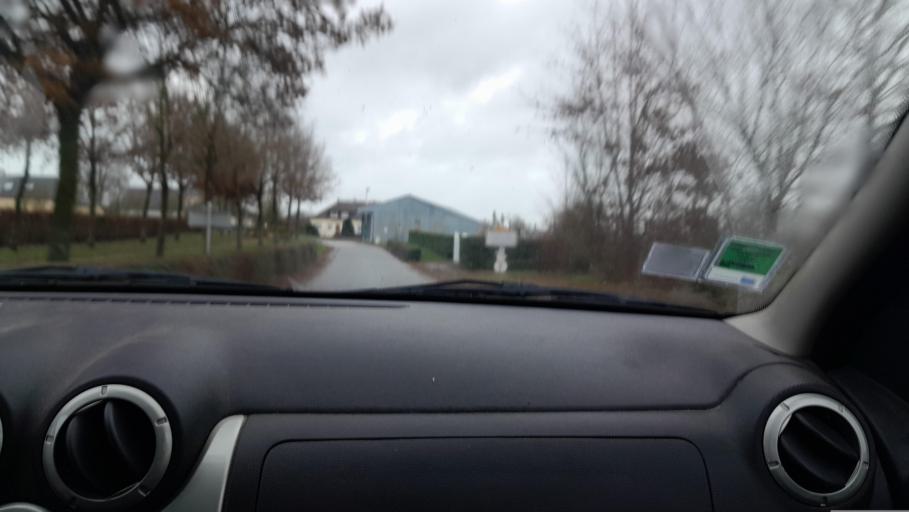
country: FR
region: Pays de la Loire
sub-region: Departement de la Mayenne
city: Ballots
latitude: 47.9074
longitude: -1.1405
